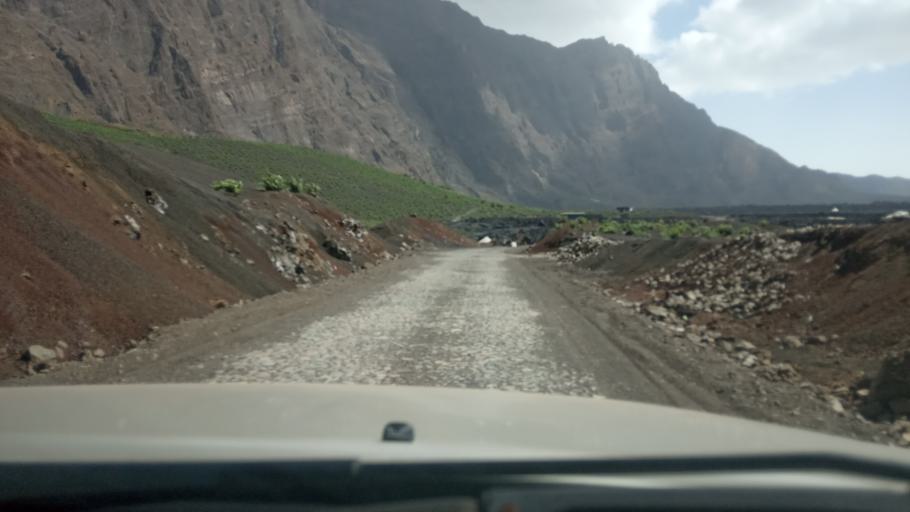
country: CV
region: Santa Catarina do Fogo
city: Cova Figueira
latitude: 14.9372
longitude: -24.3851
